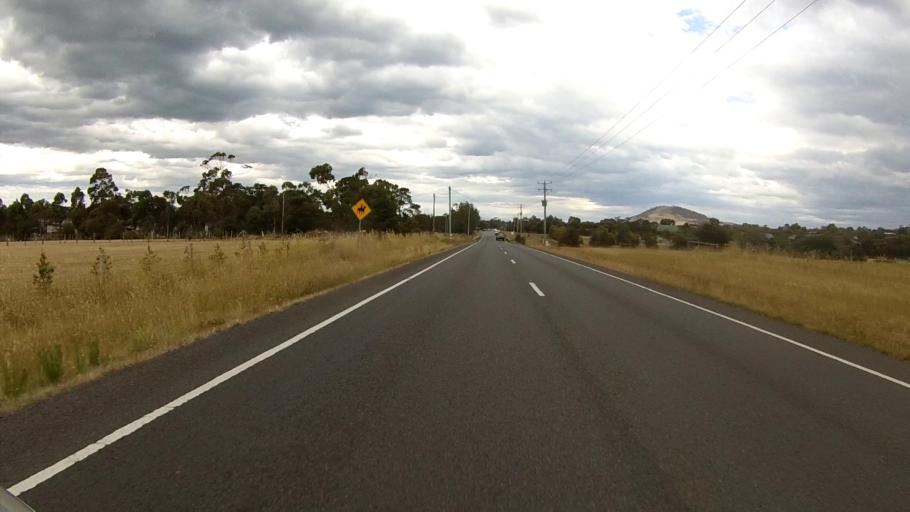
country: AU
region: Tasmania
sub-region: Clarence
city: Cambridge
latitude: -42.8418
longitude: 147.4712
